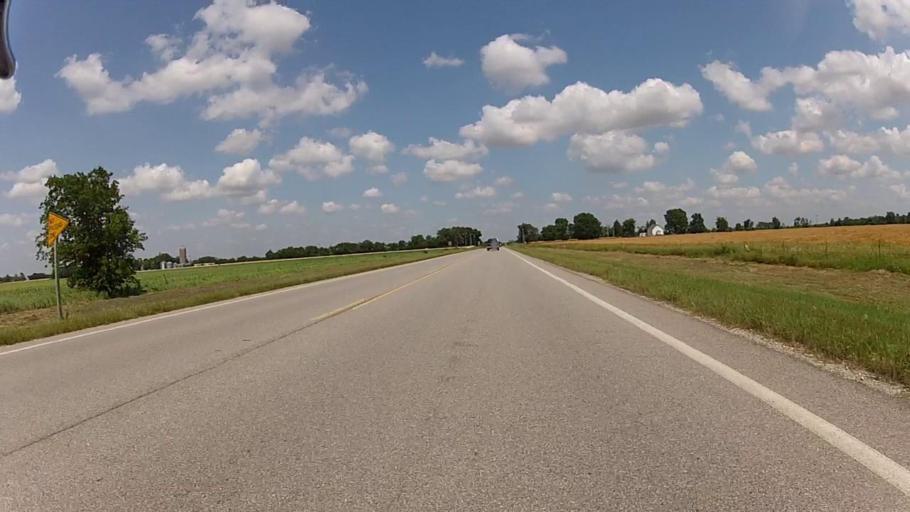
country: US
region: Kansas
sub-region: Labette County
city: Altamont
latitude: 37.1936
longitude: -95.2163
